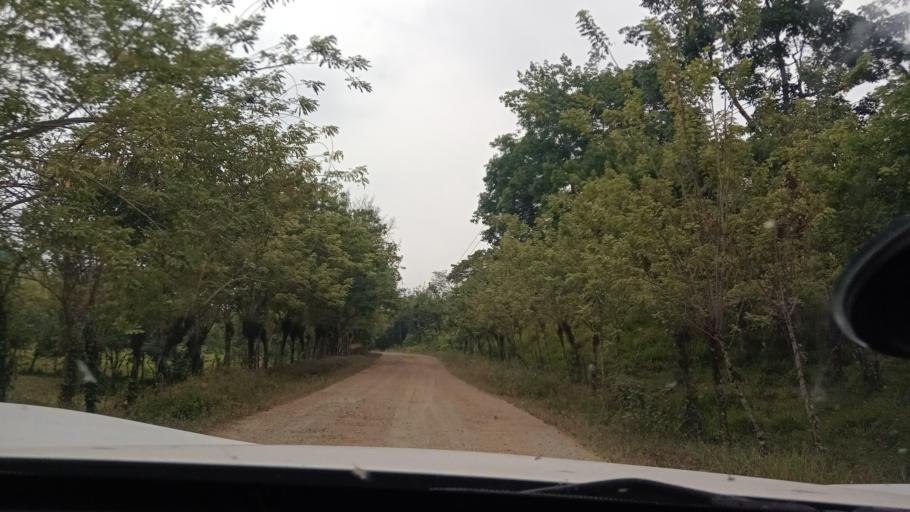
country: MX
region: Veracruz
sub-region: Uxpanapa
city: Poblado 10
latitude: 17.4563
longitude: -94.0972
